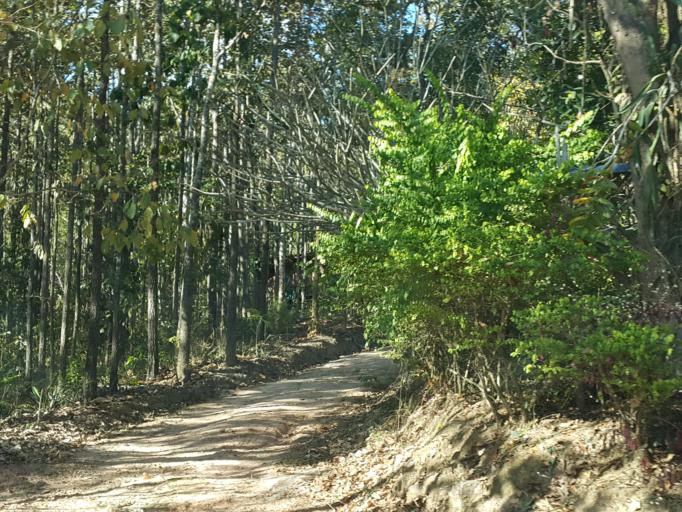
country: TH
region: Chiang Mai
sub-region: Amphoe Chiang Dao
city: Chiang Dao
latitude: 19.4738
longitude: 98.9457
